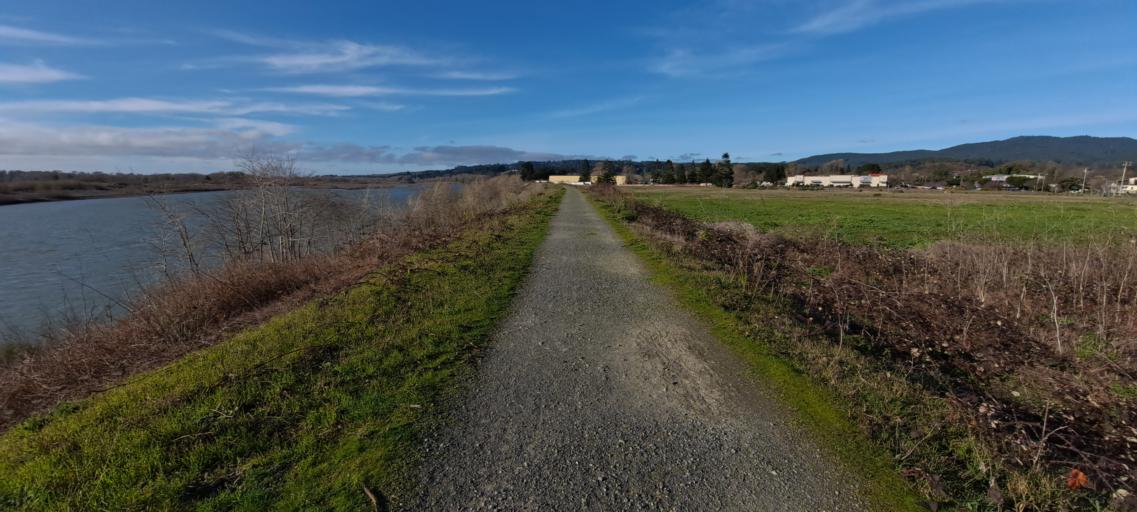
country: US
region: California
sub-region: Humboldt County
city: Fortuna
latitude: 40.5808
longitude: -124.1564
